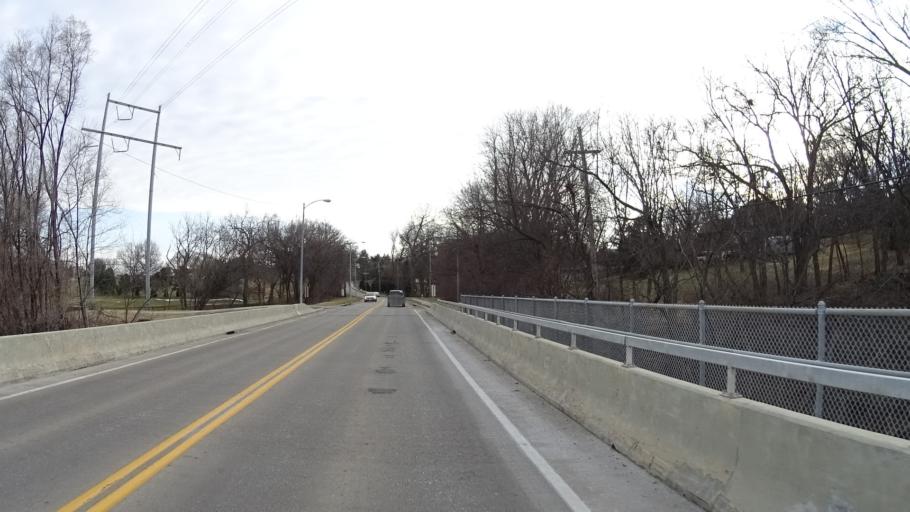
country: US
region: Nebraska
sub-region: Douglas County
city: Ralston
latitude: 41.2477
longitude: -96.0768
